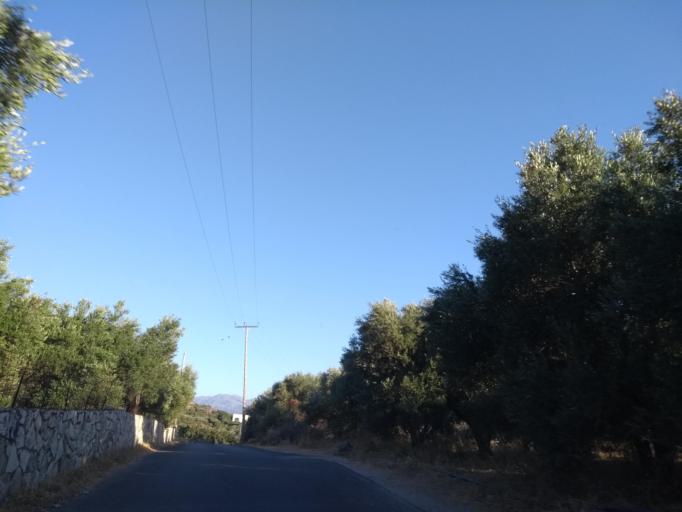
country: GR
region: Crete
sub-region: Nomos Chanias
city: Kalivai
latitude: 35.4344
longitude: 24.1752
